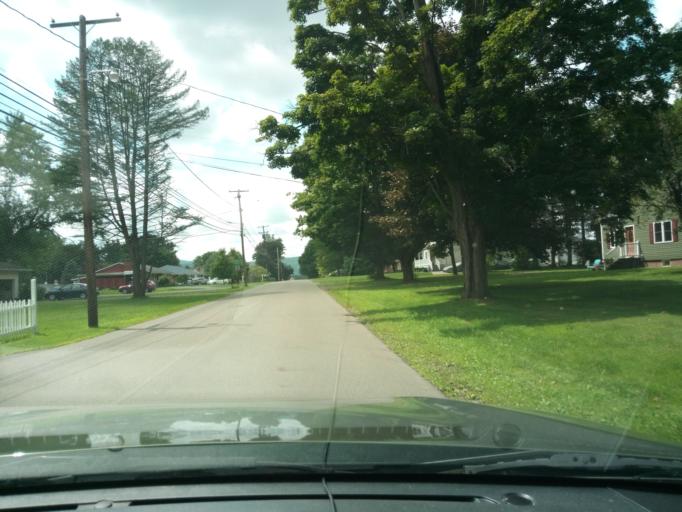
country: US
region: Pennsylvania
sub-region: Bradford County
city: South Waverly
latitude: 41.9835
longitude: -76.5362
